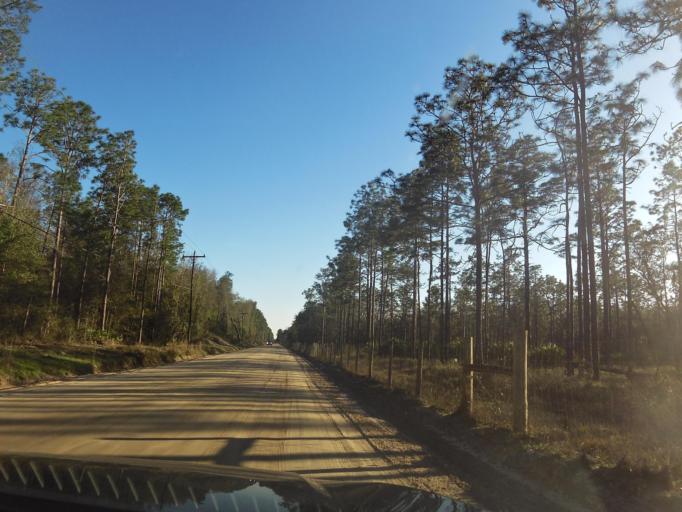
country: US
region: Florida
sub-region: Clay County
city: Middleburg
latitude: 30.1284
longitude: -81.8819
